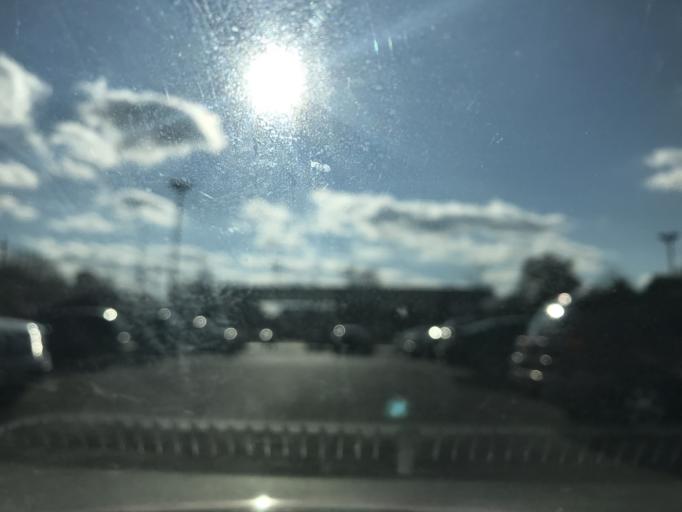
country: US
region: Kentucky
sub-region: Jefferson County
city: Audubon Park
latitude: 38.2255
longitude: -85.7309
